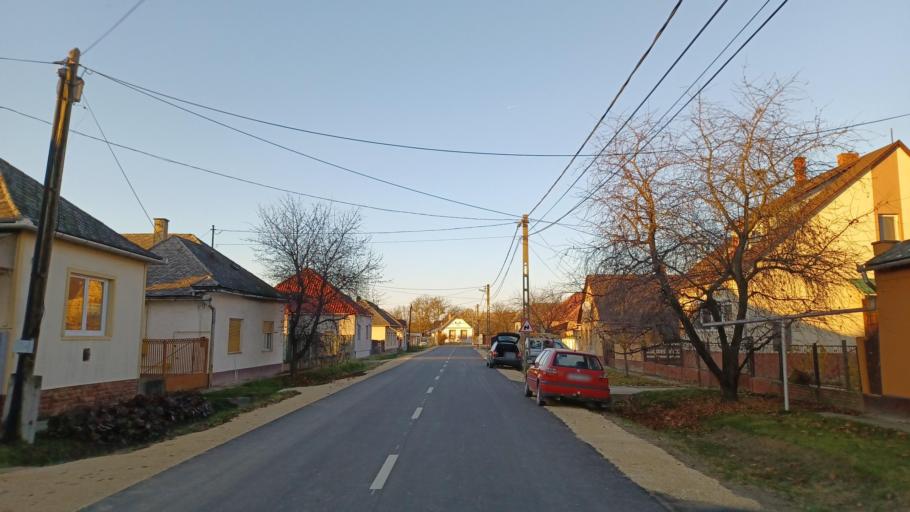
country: HU
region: Bacs-Kiskun
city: Batya
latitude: 46.4964
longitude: 18.9044
